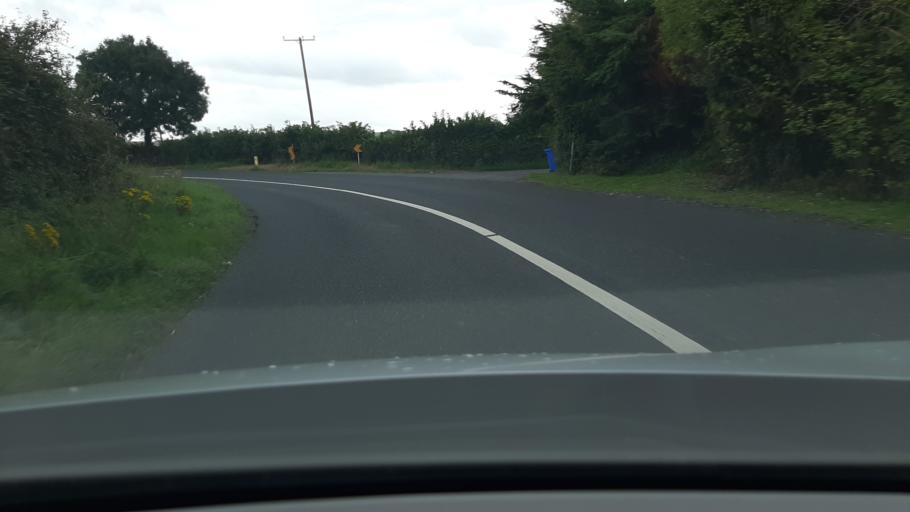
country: IE
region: Leinster
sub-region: Kildare
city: Rathangan
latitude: 53.2088
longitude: -6.9644
